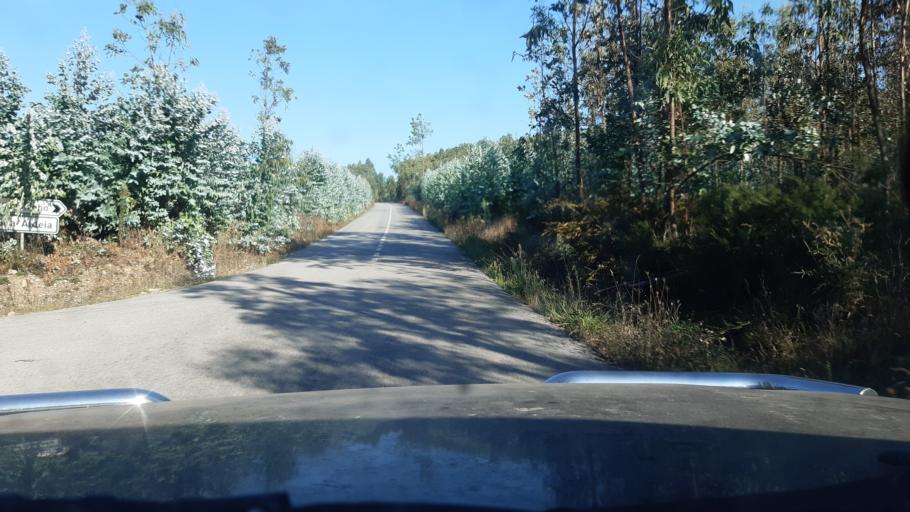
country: PT
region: Aveiro
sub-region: Agueda
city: Aguada de Cima
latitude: 40.5658
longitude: -8.3178
